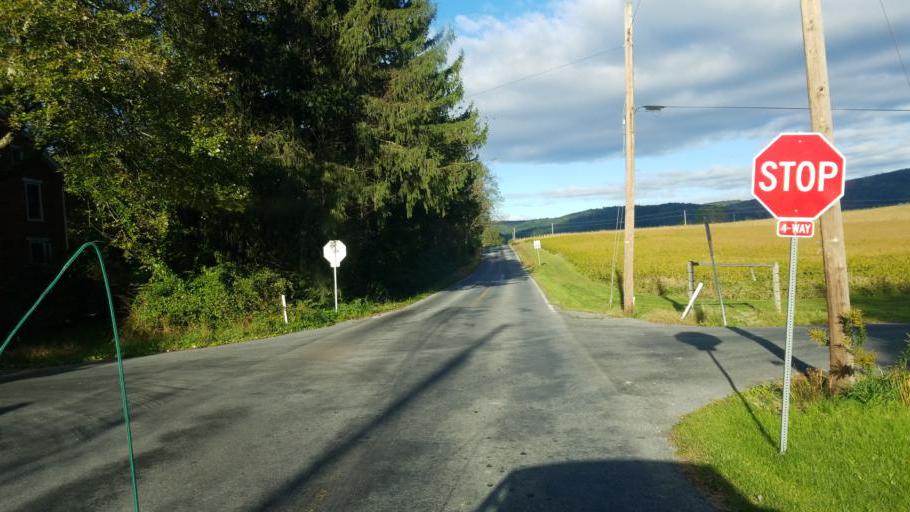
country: US
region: Pennsylvania
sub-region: Adams County
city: Biglerville
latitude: 39.8862
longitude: -77.3375
